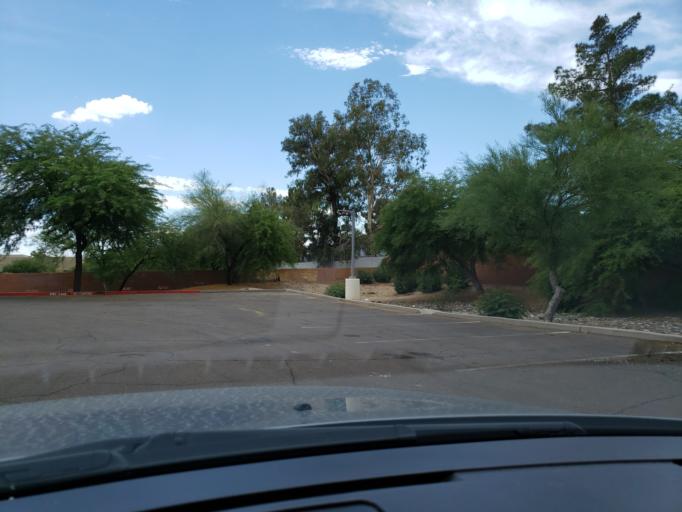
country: US
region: Arizona
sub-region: Maricopa County
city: Paradise Valley
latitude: 33.6243
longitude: -111.9797
